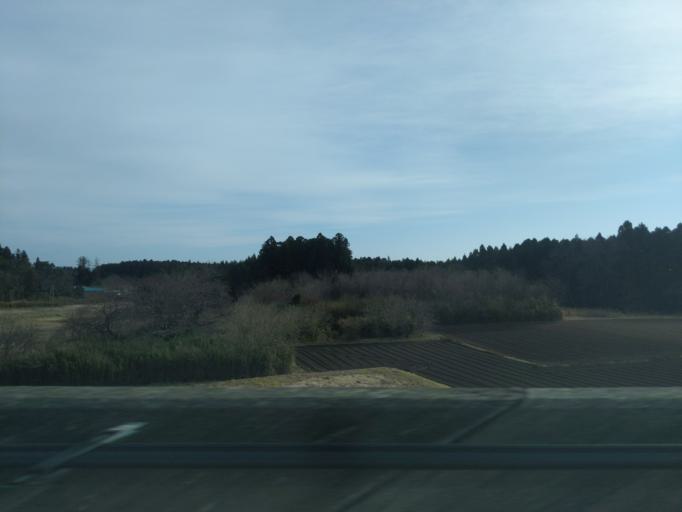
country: JP
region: Miyagi
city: Furukawa
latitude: 38.6399
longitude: 141.0101
